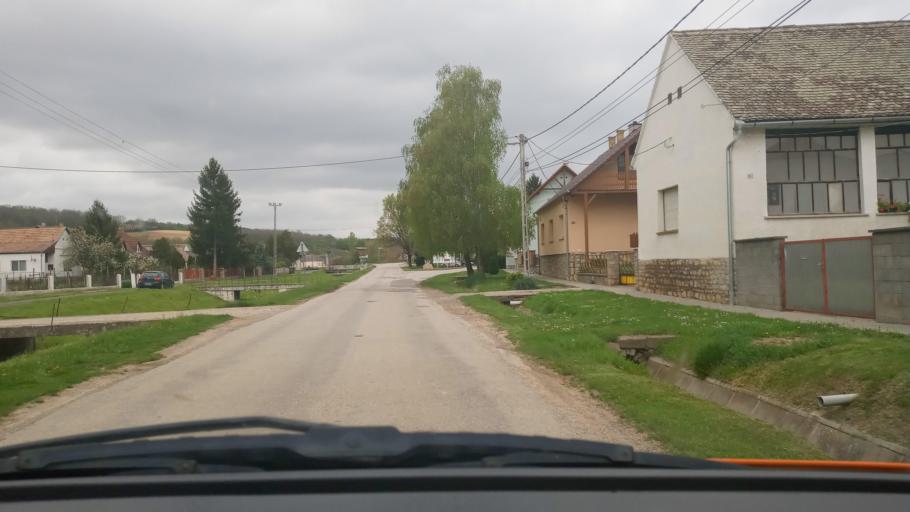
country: HU
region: Baranya
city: Boly
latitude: 46.0046
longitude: 18.5515
